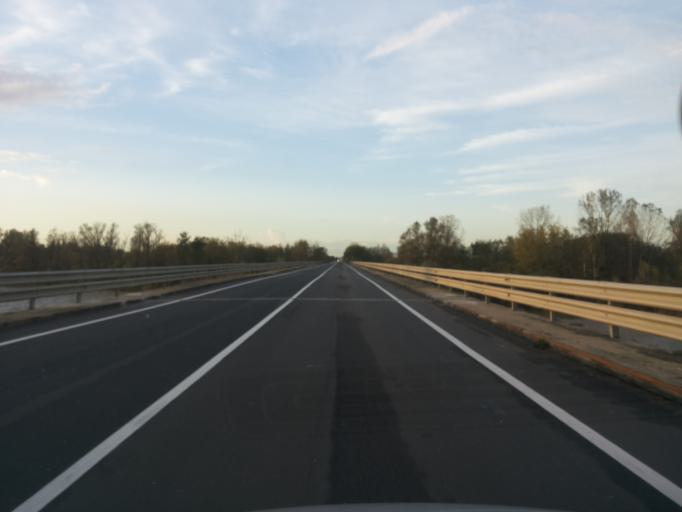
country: IT
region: Piedmont
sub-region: Provincia di Alessandria
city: Pontestura
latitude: 45.1468
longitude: 8.3407
